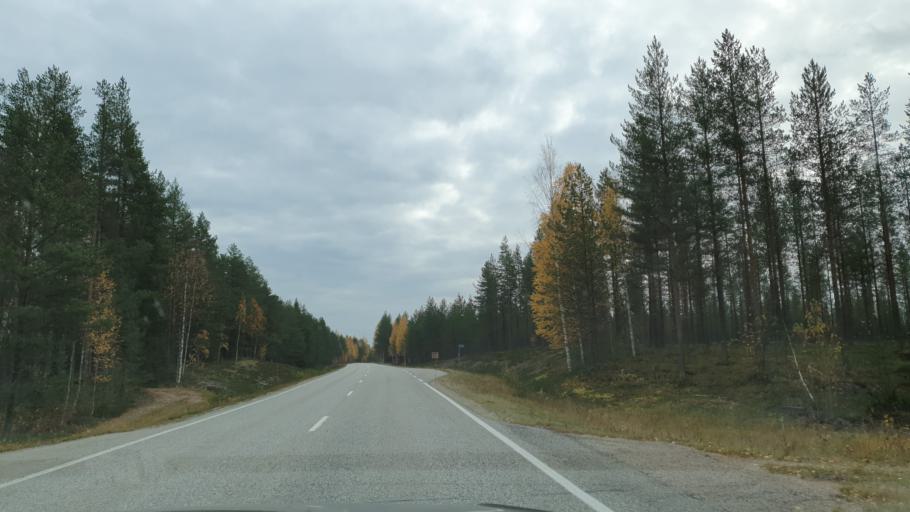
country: FI
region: Kainuu
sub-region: Kehys-Kainuu
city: Puolanka
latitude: 65.2403
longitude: 27.5845
